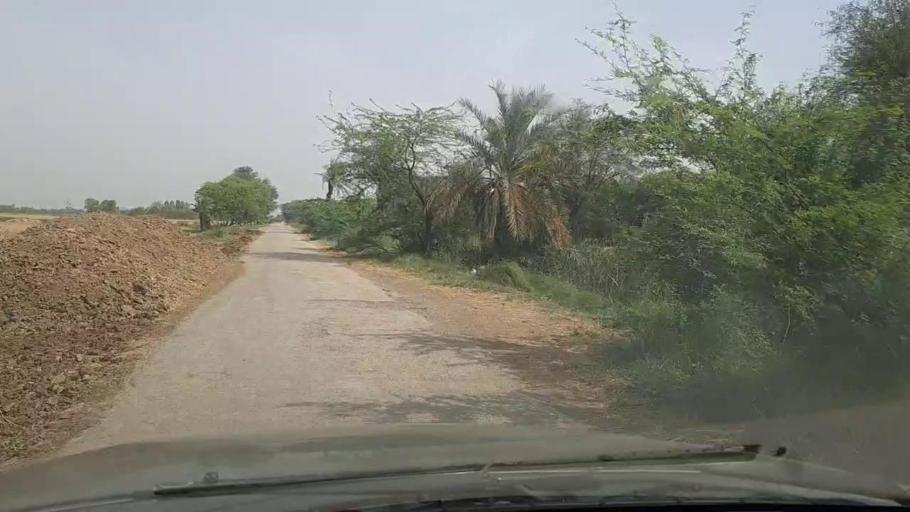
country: PK
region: Sindh
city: Lakhi
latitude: 27.8406
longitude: 68.7628
